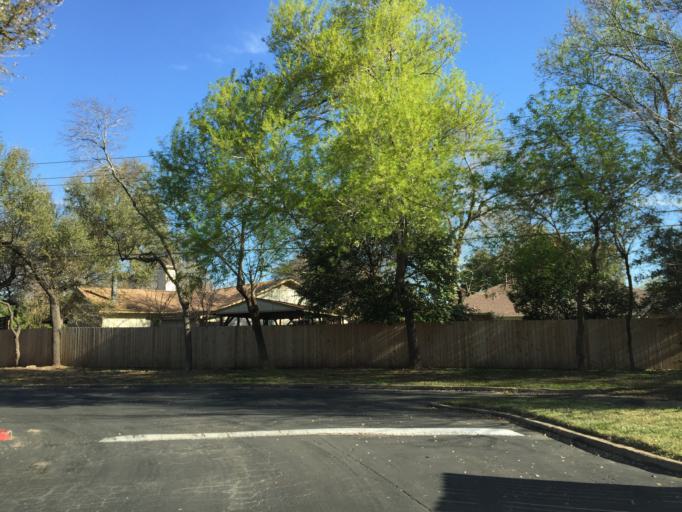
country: US
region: Texas
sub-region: Williamson County
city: Jollyville
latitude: 30.4107
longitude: -97.7412
